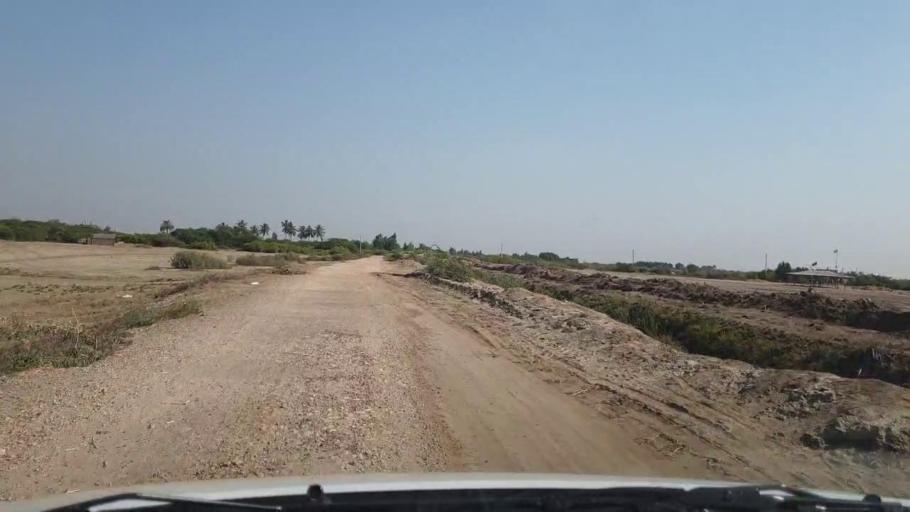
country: PK
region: Sindh
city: Mirpur Sakro
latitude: 24.6475
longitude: 67.6328
